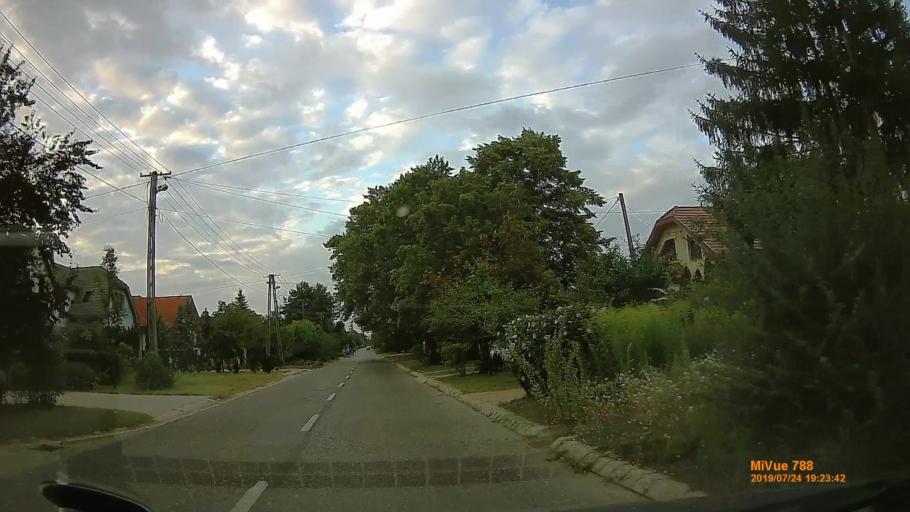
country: HU
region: Szabolcs-Szatmar-Bereg
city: Kotaj
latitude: 48.0033
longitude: 21.7321
